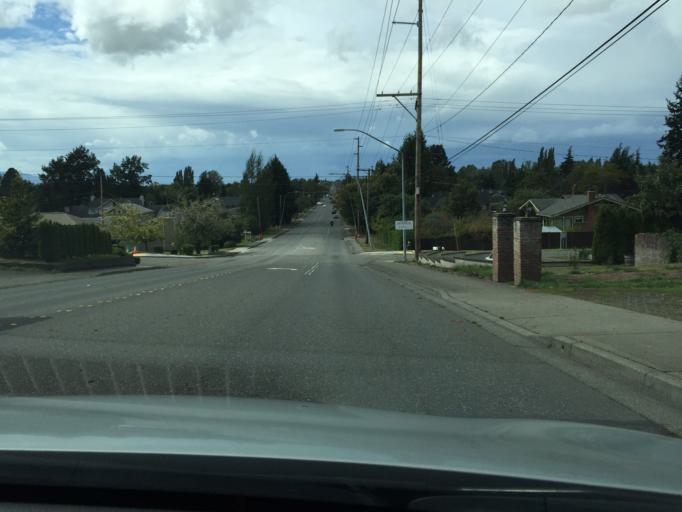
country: US
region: Washington
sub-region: Whatcom County
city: Geneva
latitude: 48.7631
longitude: -122.4364
